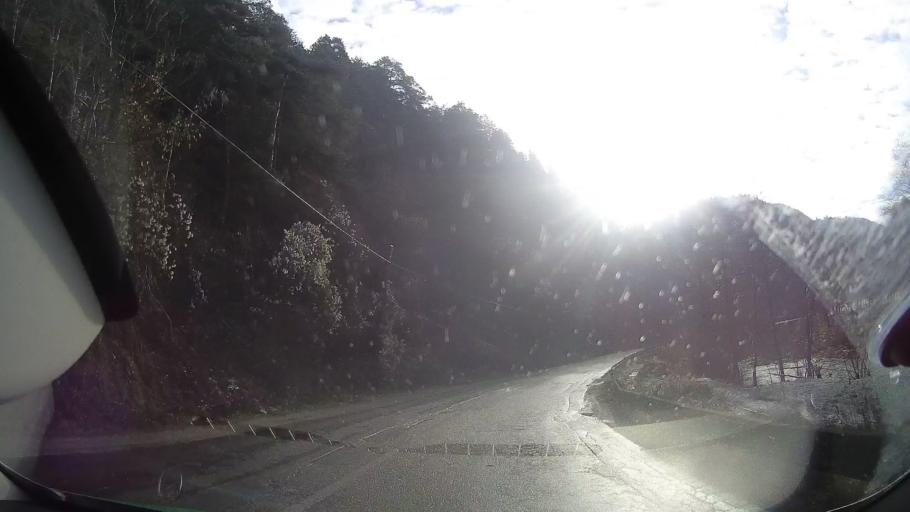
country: RO
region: Alba
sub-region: Comuna Bistra
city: Bistra
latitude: 46.3816
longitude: 23.1450
